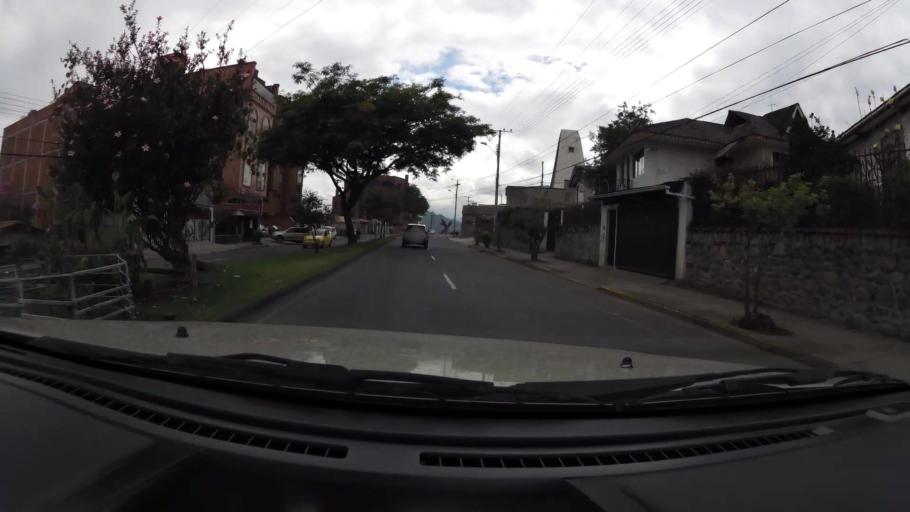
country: EC
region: Azuay
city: Cuenca
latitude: -2.9104
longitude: -79.0114
